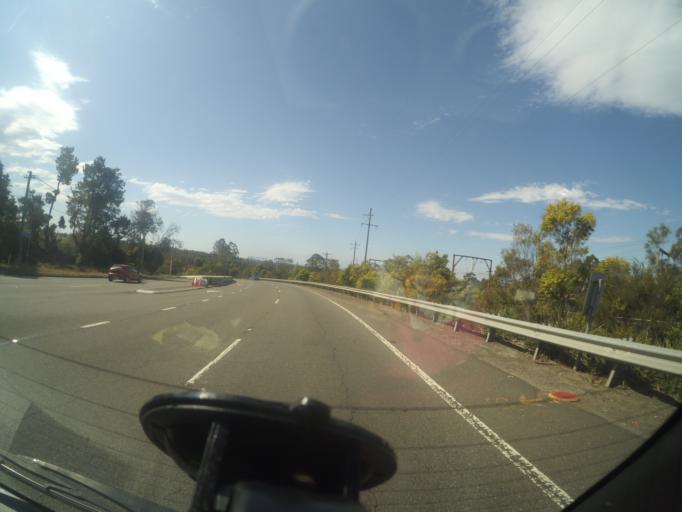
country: AU
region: New South Wales
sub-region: Blue Mountains Municipality
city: Hazelbrook
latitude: -33.7059
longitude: 150.5279
